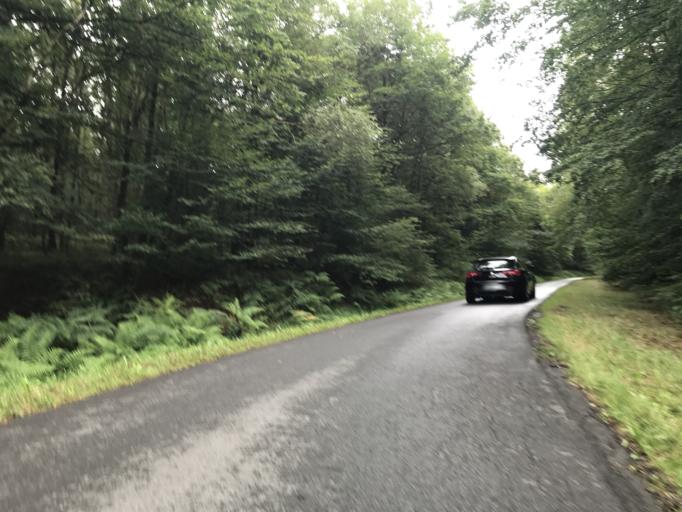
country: FR
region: Champagne-Ardenne
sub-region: Departement des Ardennes
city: Thilay
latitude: 49.8948
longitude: 4.7717
